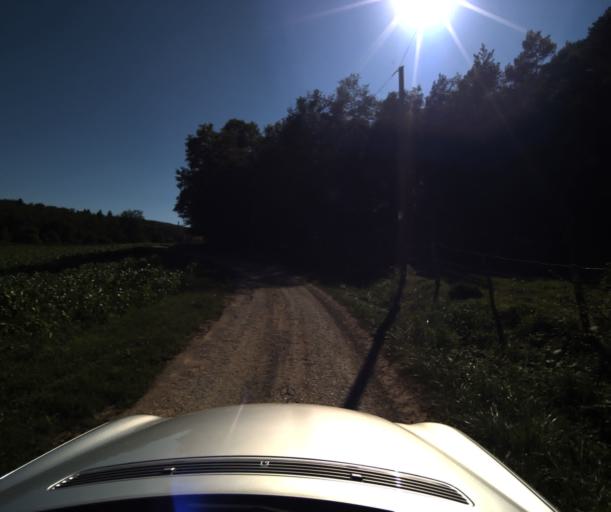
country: FR
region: Midi-Pyrenees
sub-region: Departement de l'Ariege
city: Lavelanet
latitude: 42.9755
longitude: 1.9078
